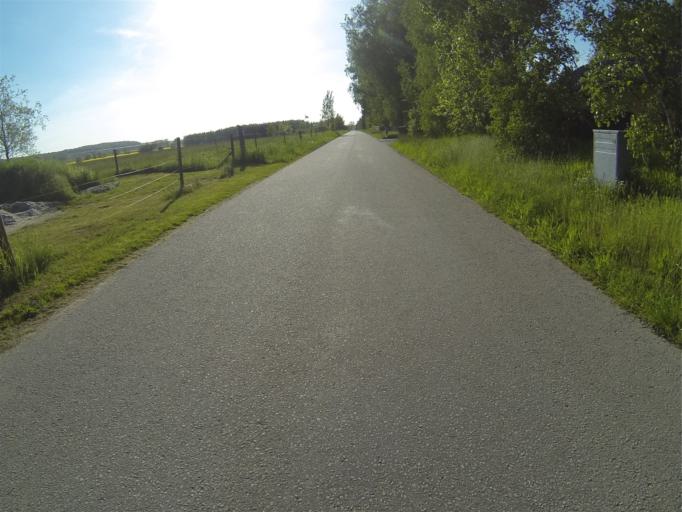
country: SE
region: Skane
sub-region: Lunds Kommun
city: Genarp
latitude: 55.7163
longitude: 13.3946
